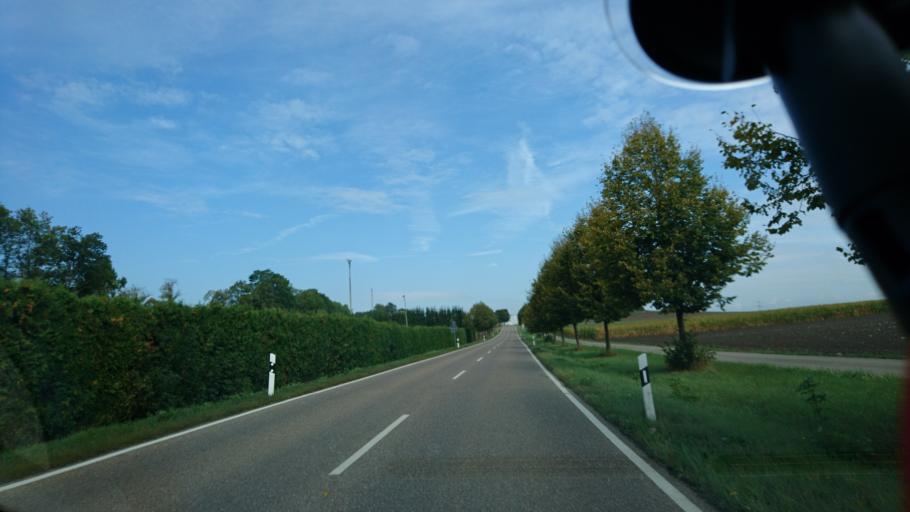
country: DE
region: Baden-Wuerttemberg
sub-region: Regierungsbezirk Stuttgart
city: Vellberg
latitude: 49.1009
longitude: 9.8824
